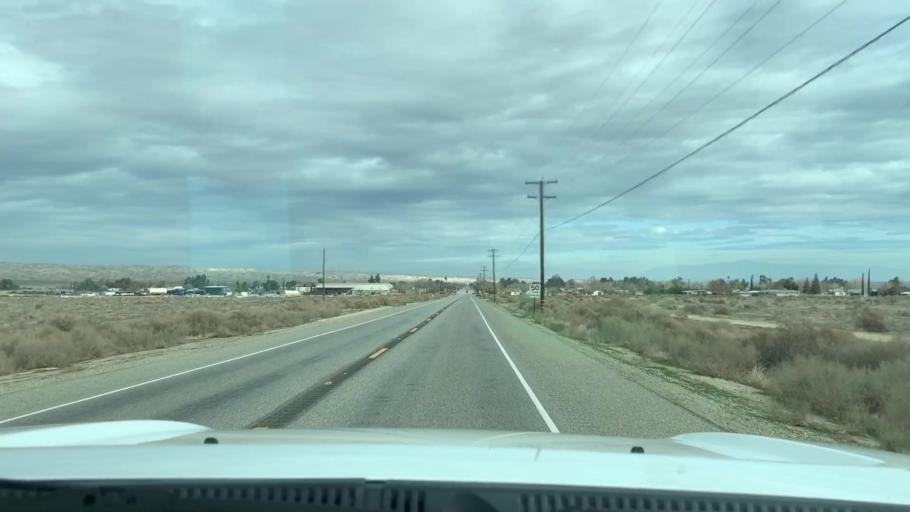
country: US
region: California
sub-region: Kern County
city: Ford City
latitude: 35.2024
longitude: -119.4159
